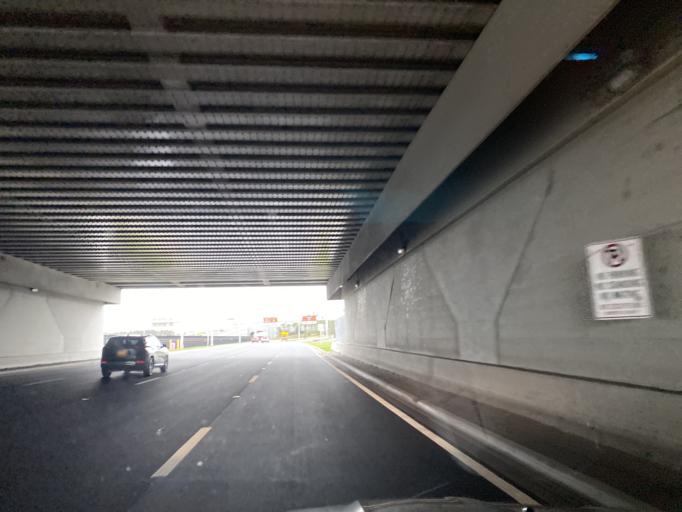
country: US
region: Florida
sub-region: Orange County
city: Taft
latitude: 28.4227
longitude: -81.3068
